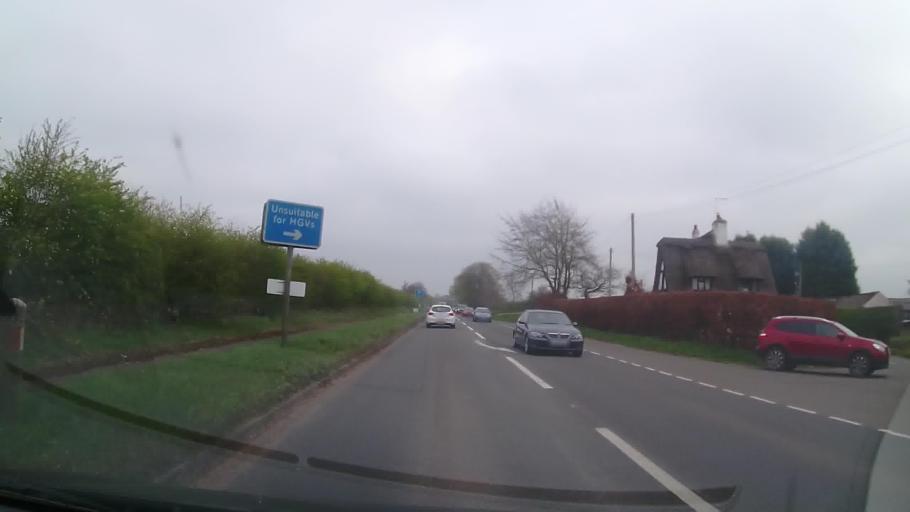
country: GB
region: England
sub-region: Shropshire
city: Market Drayton
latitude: 52.9124
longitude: -2.4569
